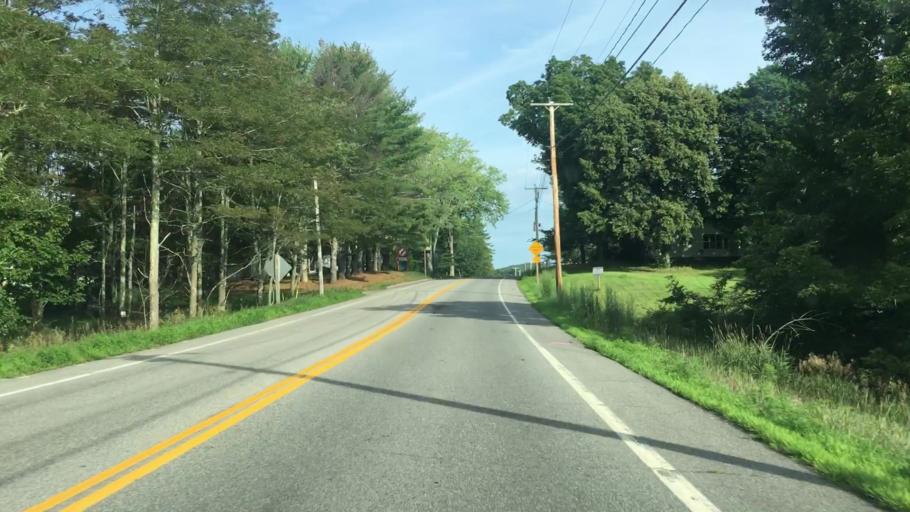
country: US
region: Maine
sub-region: York County
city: Limington
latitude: 43.7482
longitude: -70.6809
